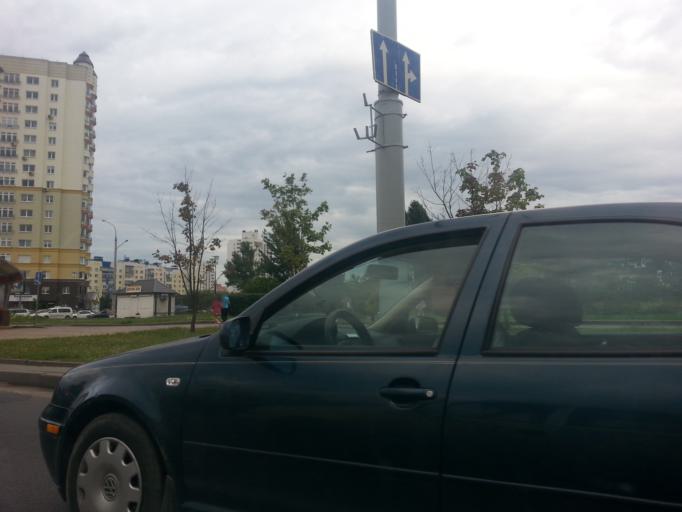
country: BY
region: Minsk
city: Novoye Medvezhino
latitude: 53.9078
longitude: 27.4719
